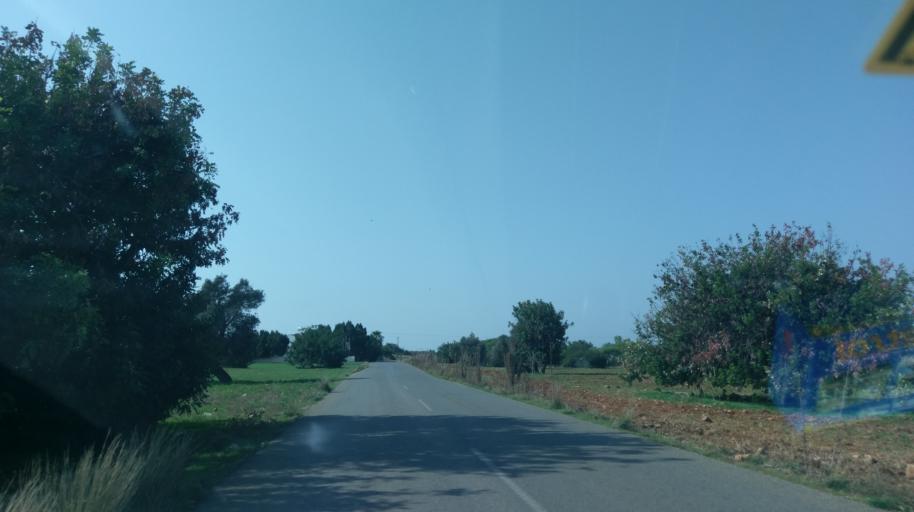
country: CY
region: Lefkosia
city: Morfou
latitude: 35.2987
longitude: 32.9755
